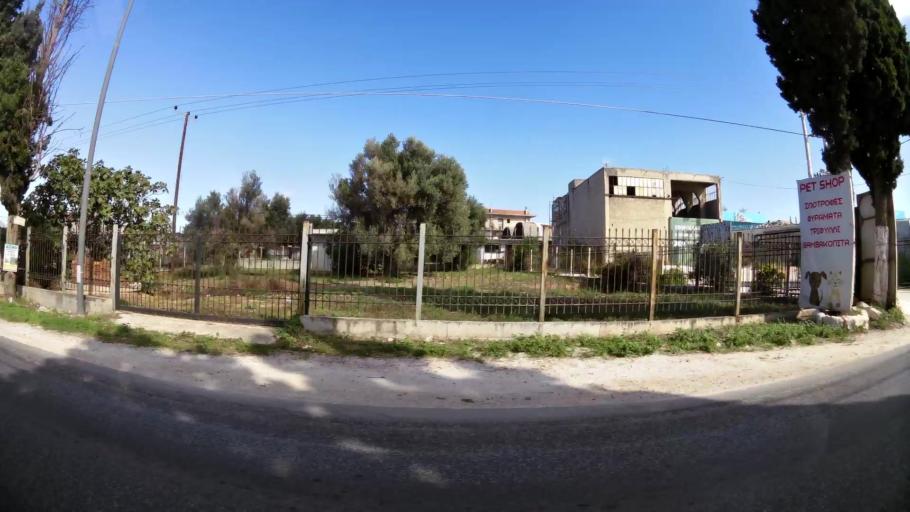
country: GR
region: Attica
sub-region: Nomarchia Anatolikis Attikis
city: Koropi
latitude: 37.8909
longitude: 23.8872
